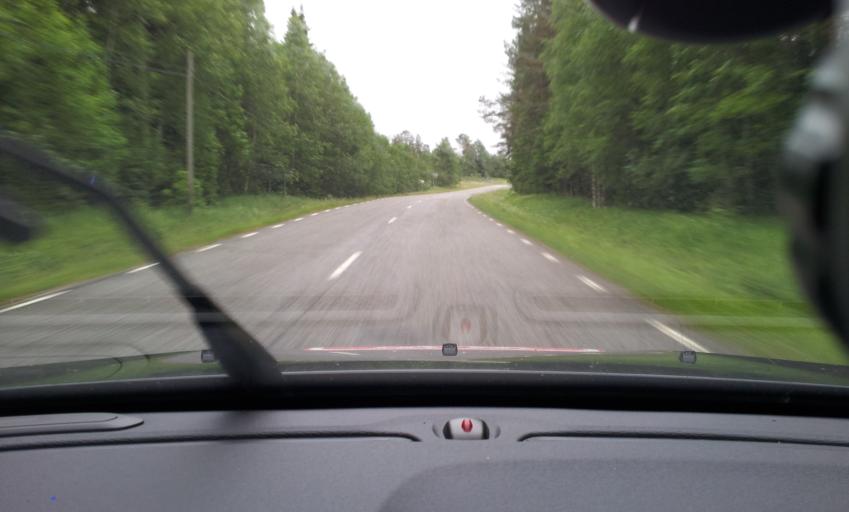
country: SE
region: Jaemtland
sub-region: Ragunda Kommun
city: Hammarstrand
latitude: 63.2338
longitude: 15.9223
